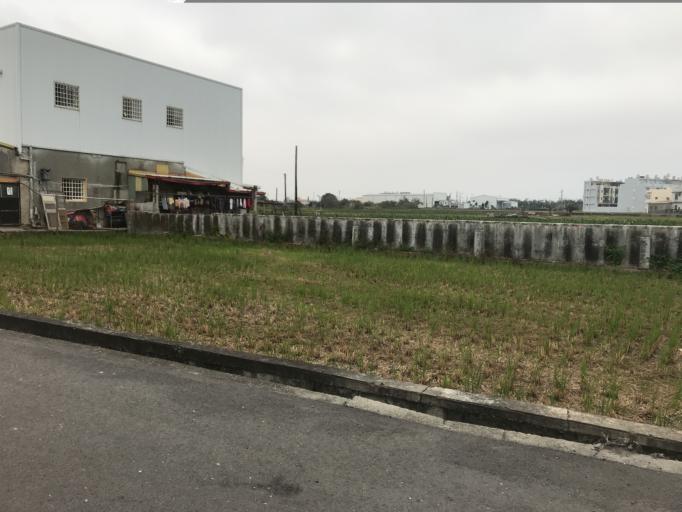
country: TW
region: Taiwan
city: Fengyuan
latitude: 24.3640
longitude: 120.6027
